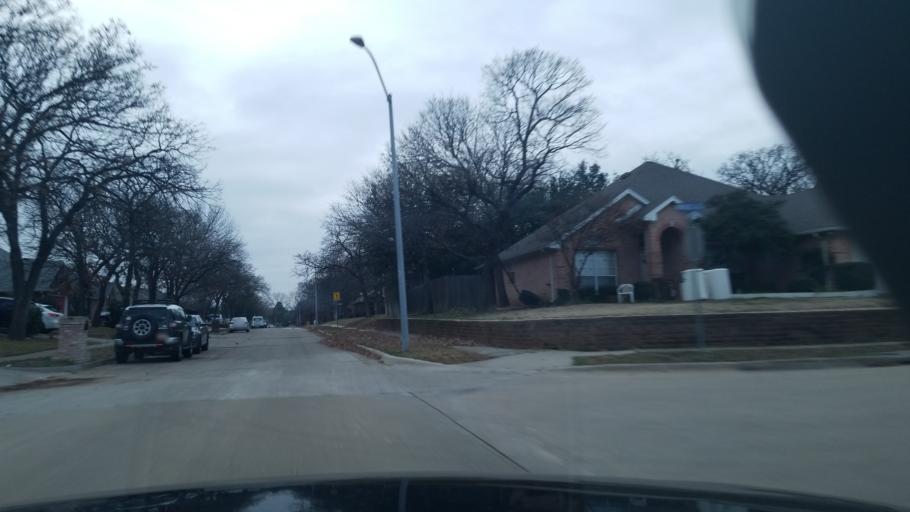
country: US
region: Texas
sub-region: Denton County
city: Corinth
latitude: 33.1358
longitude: -97.0703
